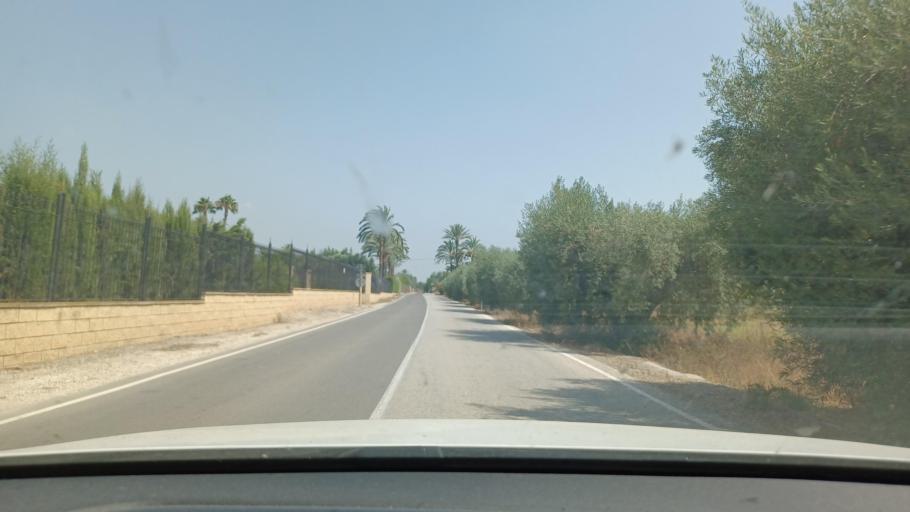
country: ES
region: Valencia
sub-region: Provincia de Alicante
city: Elche
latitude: 38.2304
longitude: -0.6939
